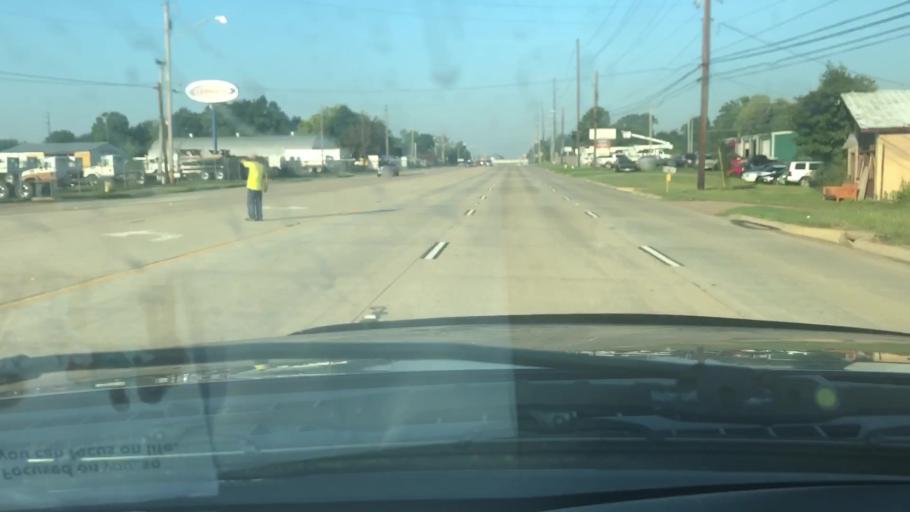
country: US
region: Texas
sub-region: Bowie County
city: Wake Village
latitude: 33.4199
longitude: -94.0879
